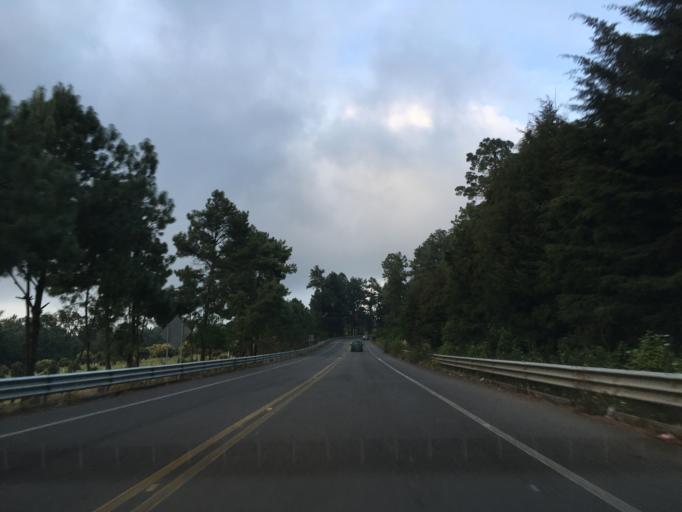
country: MX
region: Michoacan
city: Angahuan
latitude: 19.5690
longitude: -102.2749
